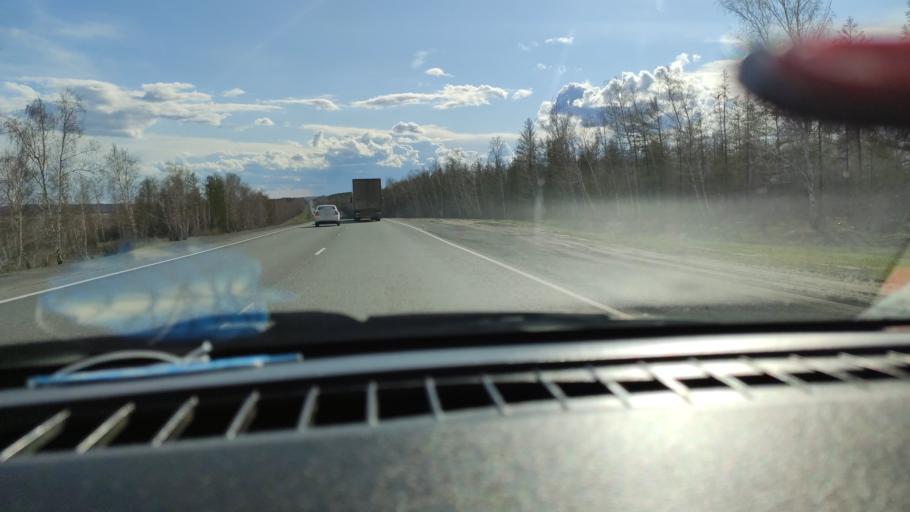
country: RU
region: Saratov
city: Sennoy
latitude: 52.1290
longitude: 46.8588
